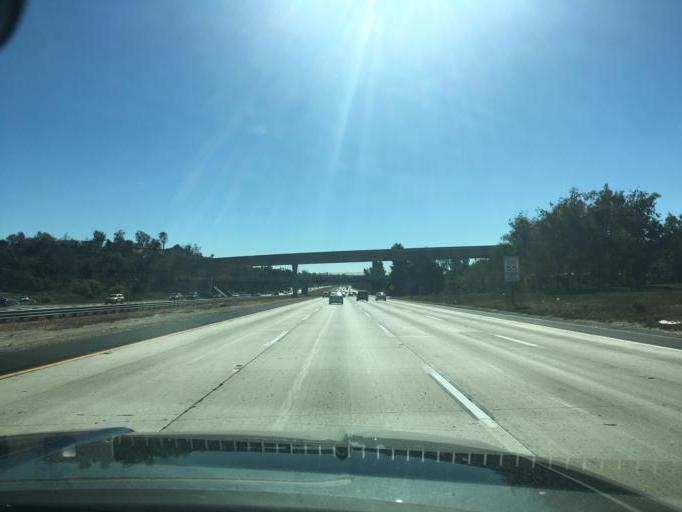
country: US
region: California
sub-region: San Diego County
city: La Mesa
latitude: 32.8258
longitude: -117.1174
